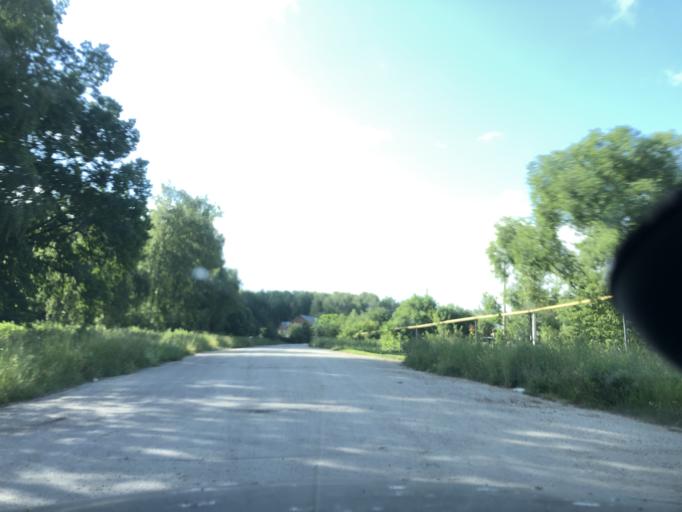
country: RU
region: Tula
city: Shvartsevskiy
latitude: 54.2505
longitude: 37.9300
